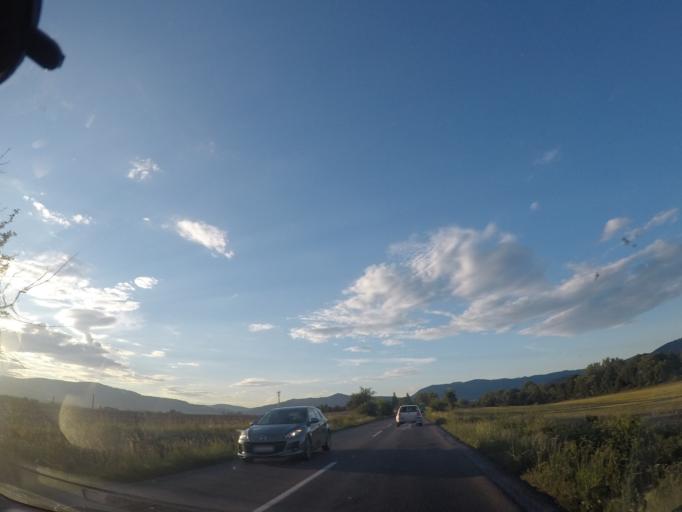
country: SK
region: Nitriansky
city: Prievidza
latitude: 48.8602
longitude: 18.6414
